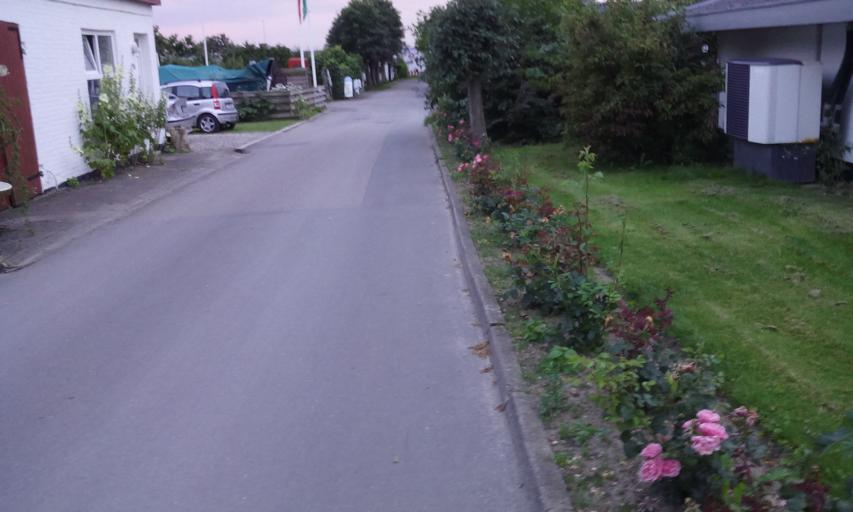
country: DK
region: South Denmark
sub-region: Sonderborg Kommune
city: Horuphav
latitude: 54.8658
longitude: 9.8920
